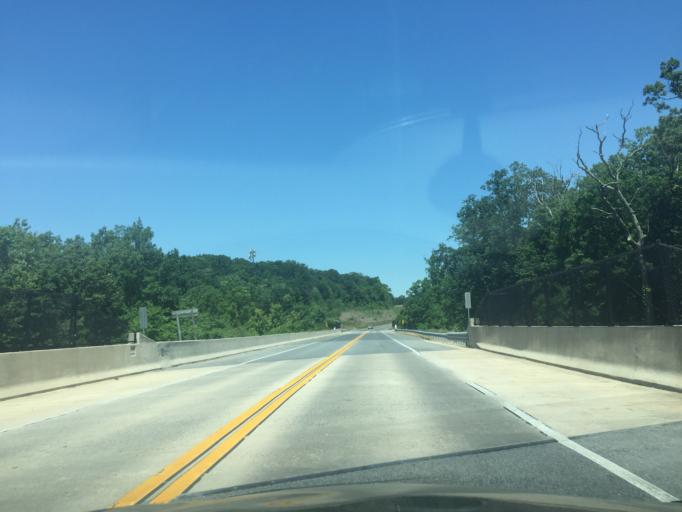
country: US
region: Maryland
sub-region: Carroll County
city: Hampstead
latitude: 39.6009
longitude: -76.8648
